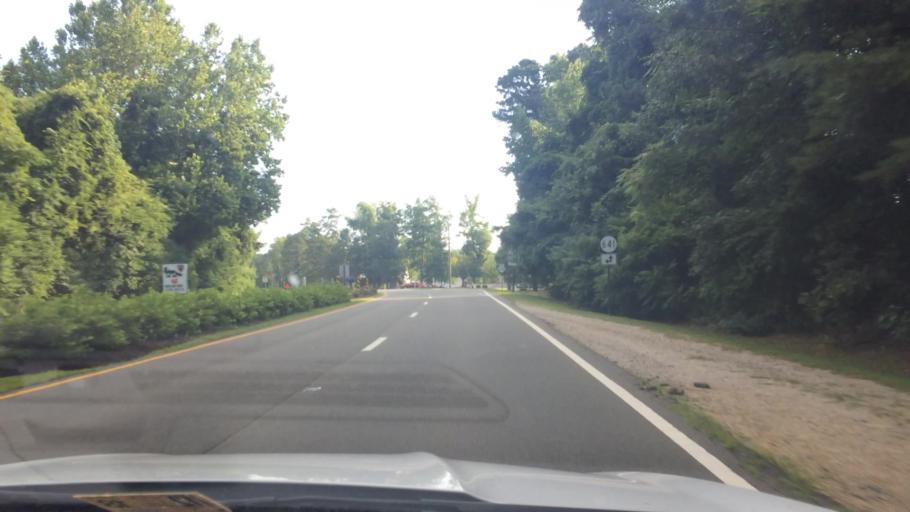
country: US
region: Virginia
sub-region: City of Williamsburg
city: Williamsburg
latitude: 37.2666
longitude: -76.6393
